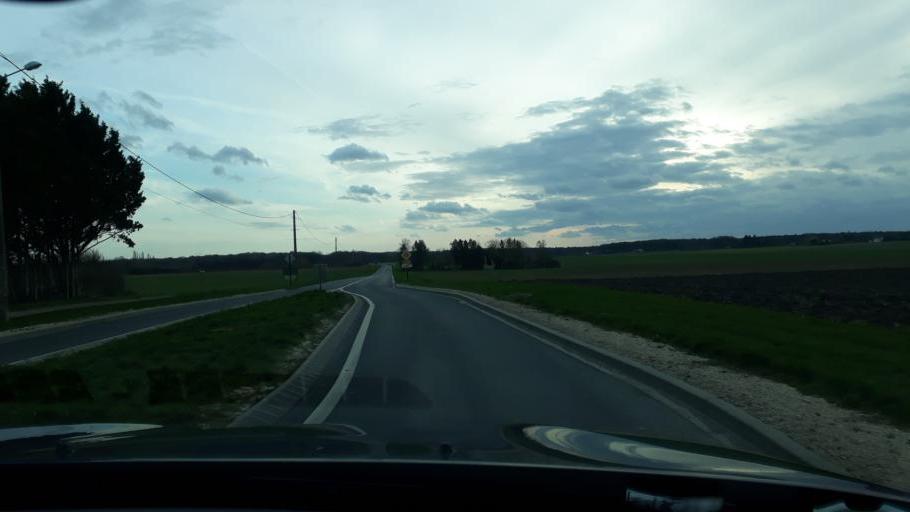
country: FR
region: Centre
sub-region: Departement du Loiret
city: Chilleurs-aux-Bois
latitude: 48.0668
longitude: 2.1319
